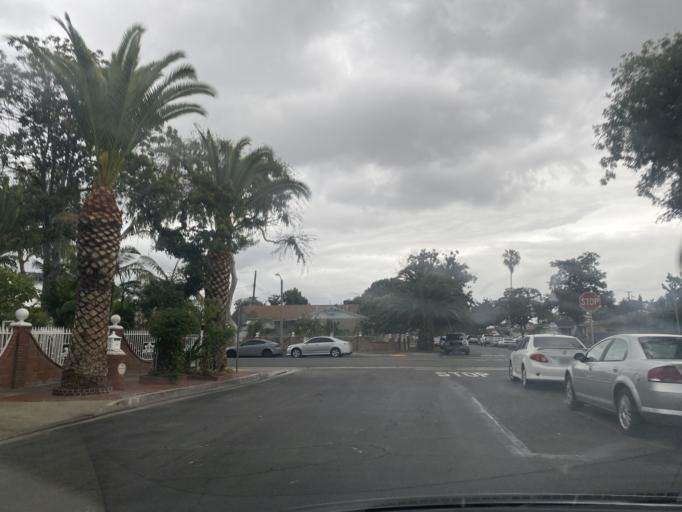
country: US
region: California
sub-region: Orange County
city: Fullerton
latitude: 33.8644
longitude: -117.9181
